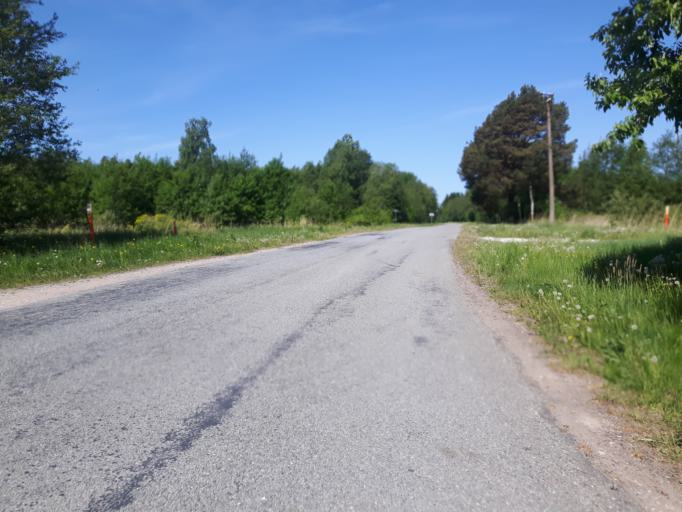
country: EE
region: Ida-Virumaa
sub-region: Aseri vald
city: Aseri
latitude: 59.4509
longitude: 26.8563
